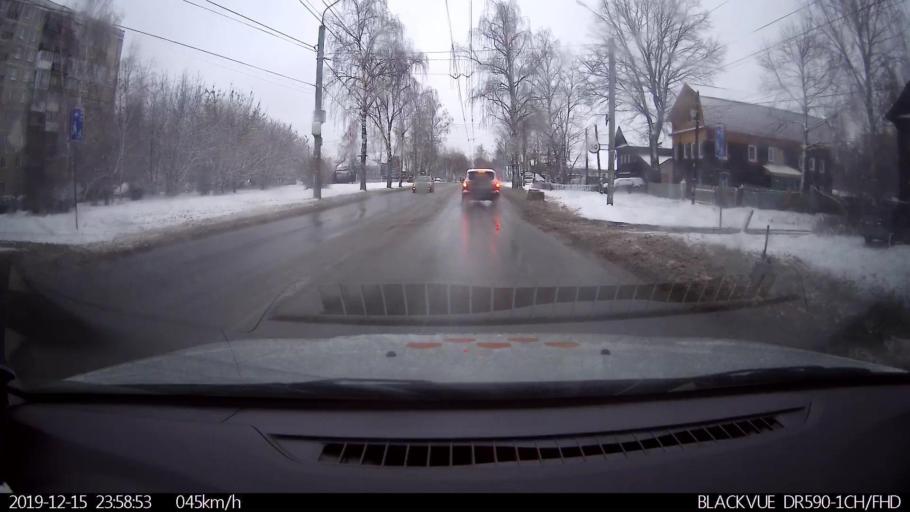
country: RU
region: Nizjnij Novgorod
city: Neklyudovo
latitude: 56.3633
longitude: 43.8552
